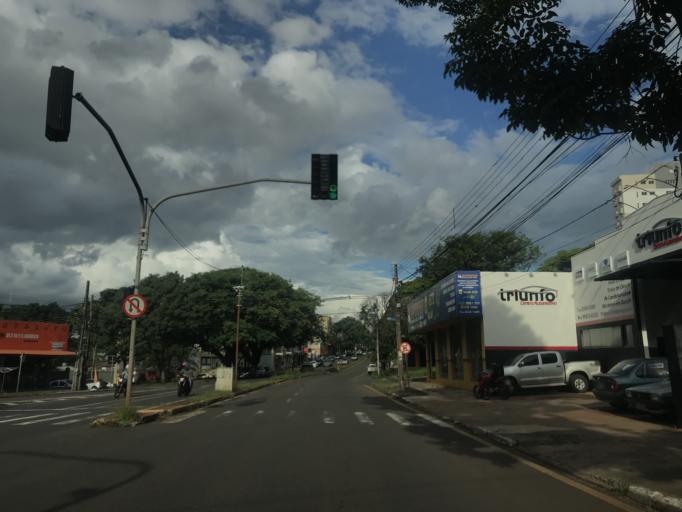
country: BR
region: Parana
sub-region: Maringa
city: Maringa
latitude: -23.4246
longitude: -51.9598
